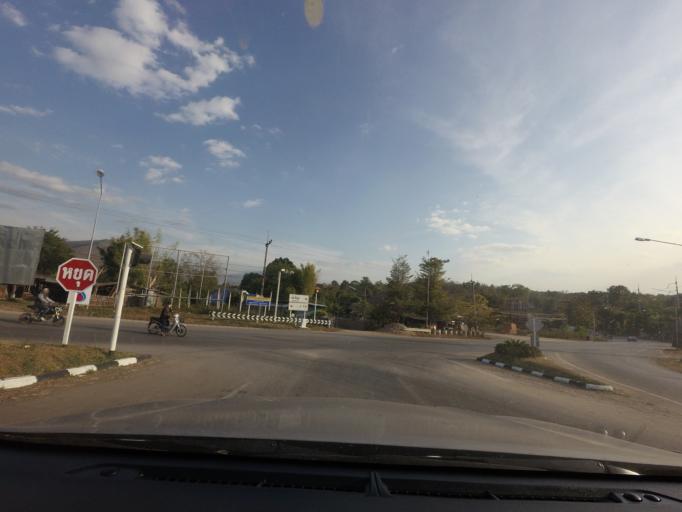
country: TH
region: Chiang Mai
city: Pai
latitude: 19.3461
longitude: 98.4331
